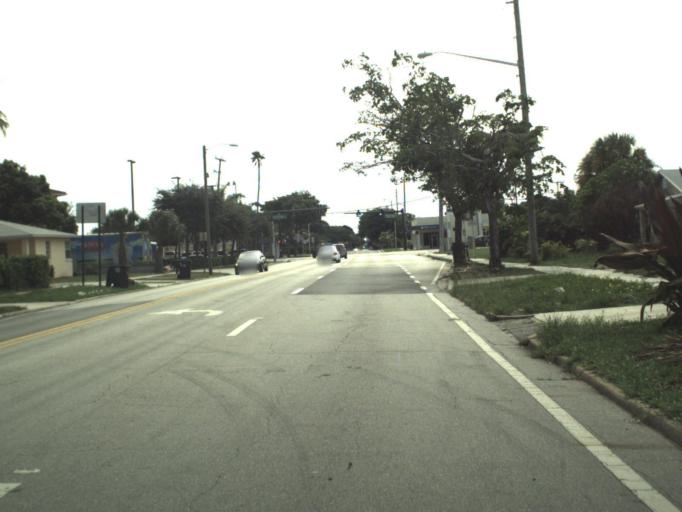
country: US
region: Florida
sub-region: Palm Beach County
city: Mangonia Park
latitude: 26.7529
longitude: -80.0576
